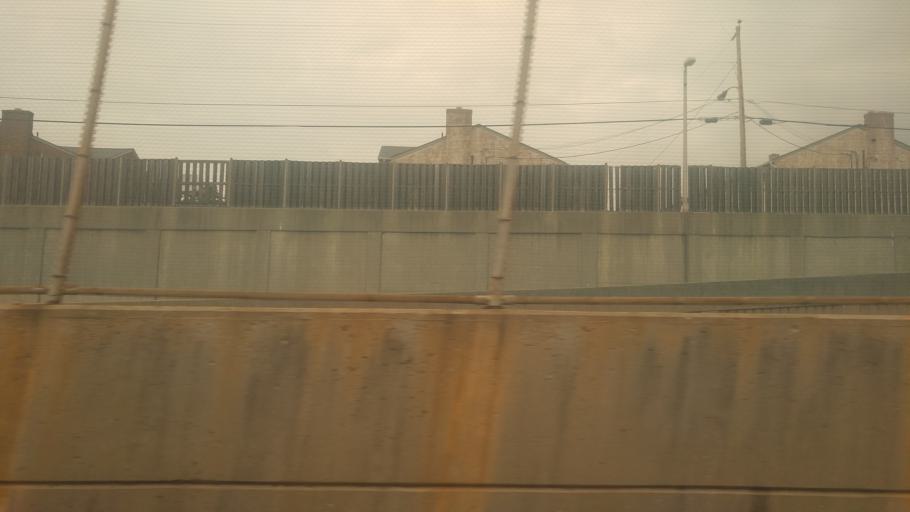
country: US
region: Virginia
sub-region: City of Richmond
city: Richmond
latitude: 37.5658
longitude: -77.4824
